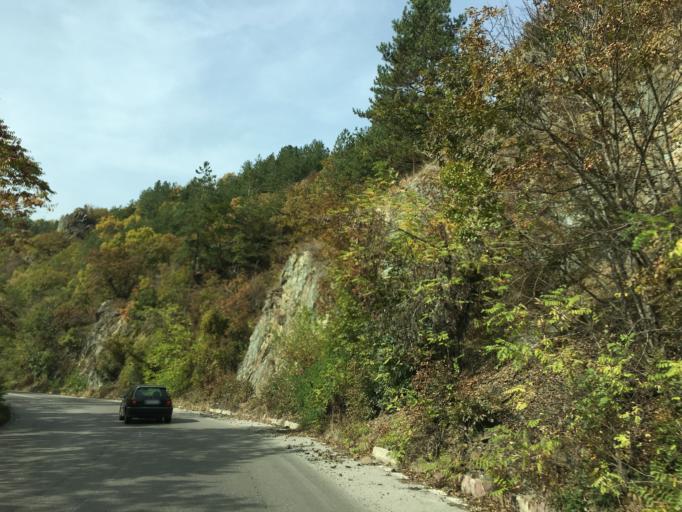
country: BG
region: Sofia-Capital
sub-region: Stolichna Obshtina
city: Sofia
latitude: 42.5686
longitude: 23.4277
